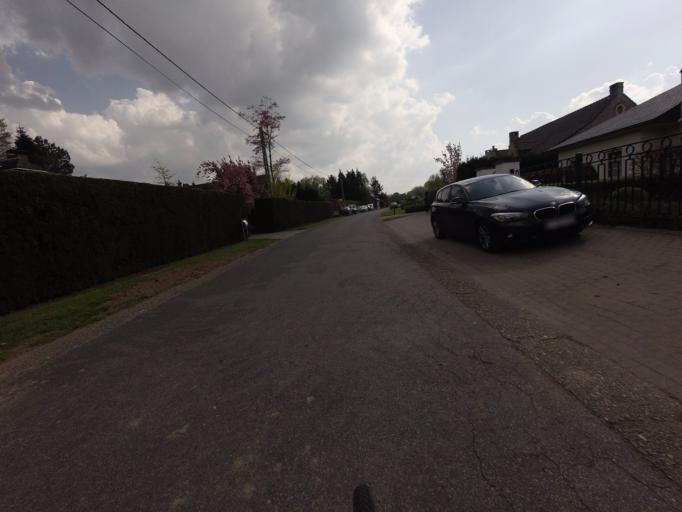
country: BE
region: Flanders
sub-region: Provincie Antwerpen
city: Berlaar
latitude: 51.0779
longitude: 4.6738
